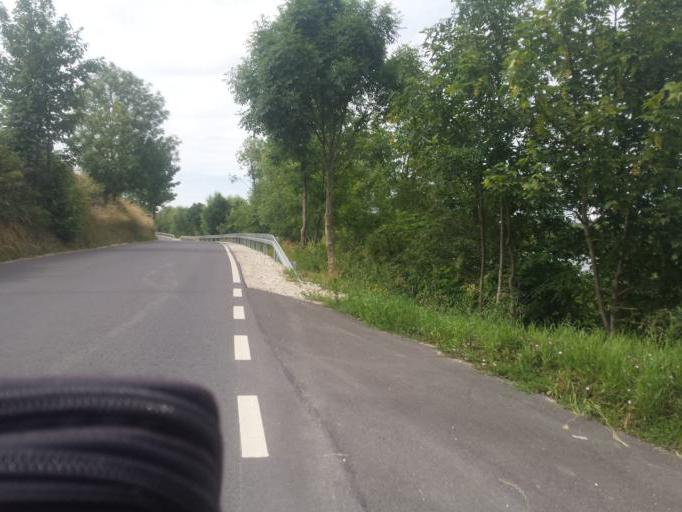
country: PL
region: Warmian-Masurian Voivodeship
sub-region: Powiat ilawski
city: Ilawa
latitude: 53.5144
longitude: 19.5645
